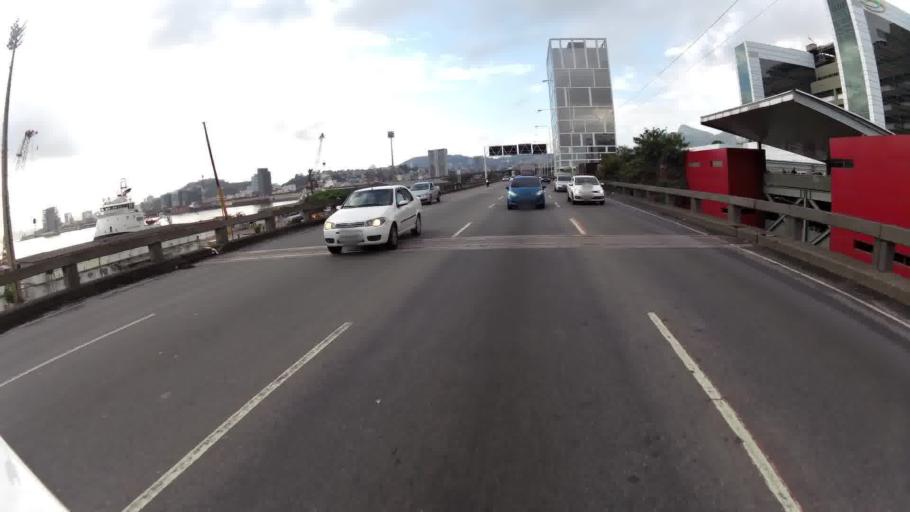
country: BR
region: Rio de Janeiro
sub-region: Rio De Janeiro
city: Rio de Janeiro
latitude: -22.8926
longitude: -43.2144
